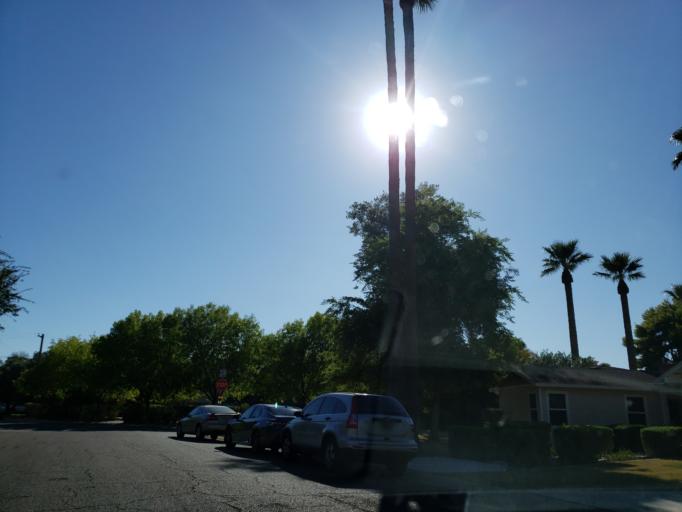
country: US
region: Arizona
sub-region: Maricopa County
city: Phoenix
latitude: 33.5226
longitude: -112.0849
